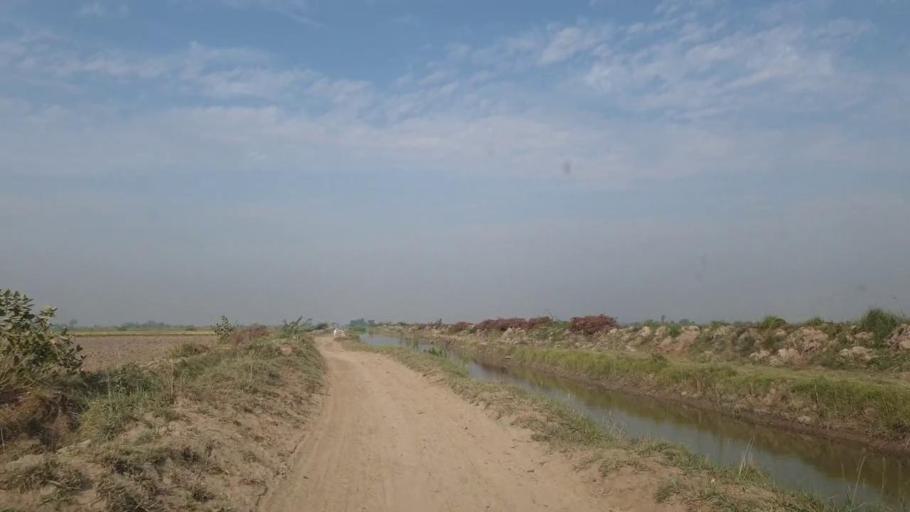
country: PK
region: Sindh
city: Tando Bago
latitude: 24.8723
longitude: 68.9672
